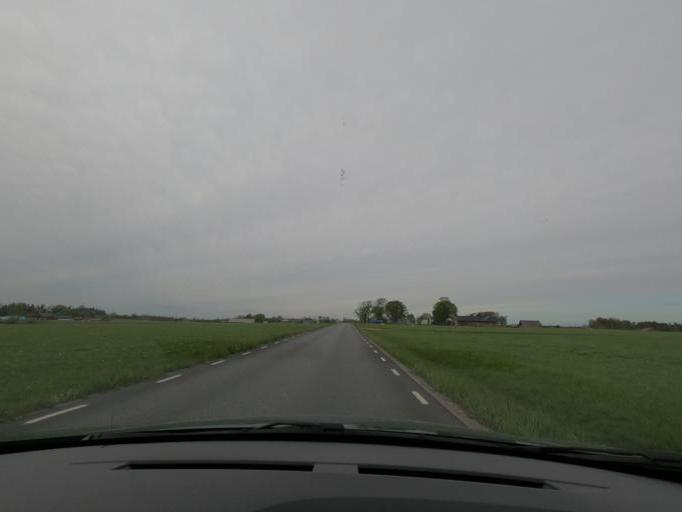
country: SE
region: Joenkoeping
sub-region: Varnamo Kommun
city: Bredaryd
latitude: 57.1386
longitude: 13.7123
